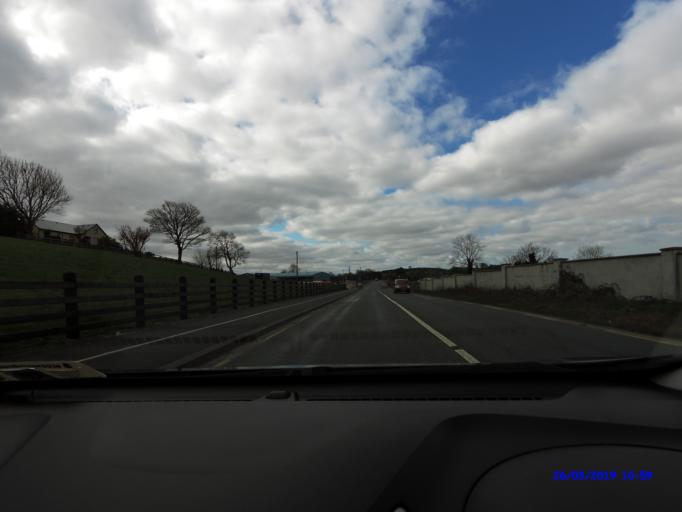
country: IE
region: Connaught
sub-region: Maigh Eo
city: Castlebar
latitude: 53.8517
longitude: -9.3402
